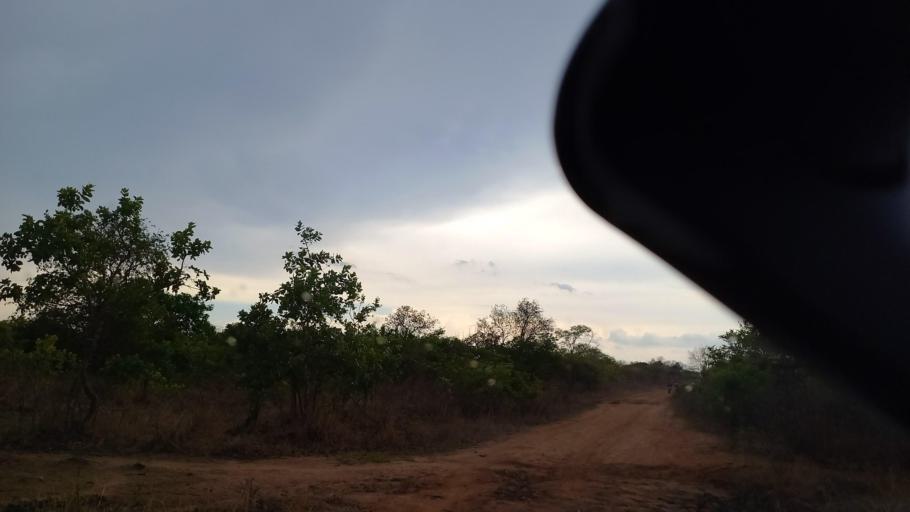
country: ZM
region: Lusaka
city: Kafue
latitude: -16.0004
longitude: 28.2800
